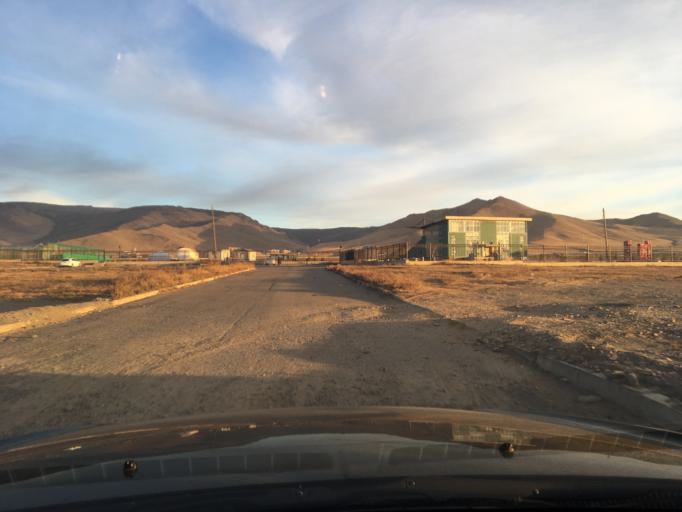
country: MN
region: Ulaanbaatar
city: Ulaanbaatar
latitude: 47.8637
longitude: 106.8075
